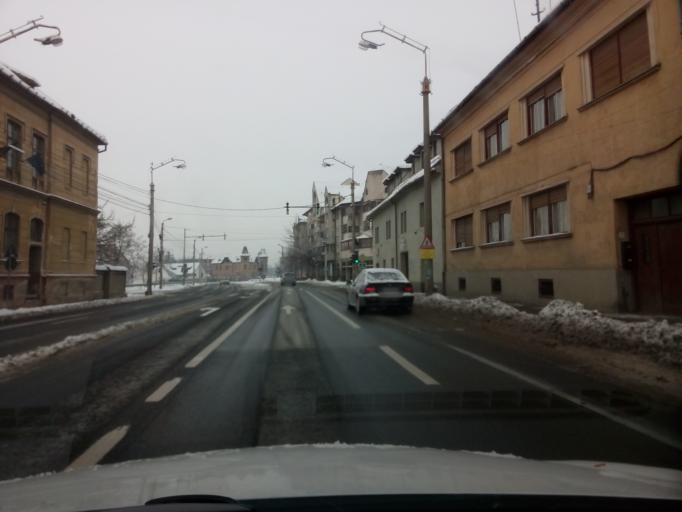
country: RO
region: Sibiu
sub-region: Municipiul Sibiu
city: Sibiu
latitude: 45.7995
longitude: 24.1573
